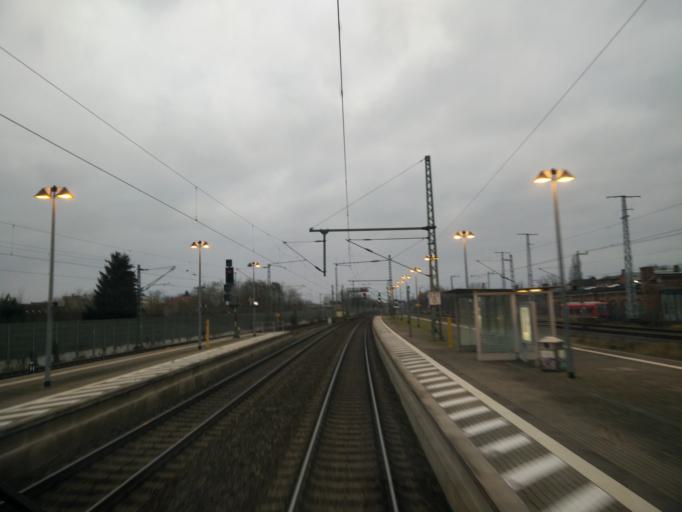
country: DE
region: Brandenburg
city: Wittenberge
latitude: 53.0052
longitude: 11.7623
